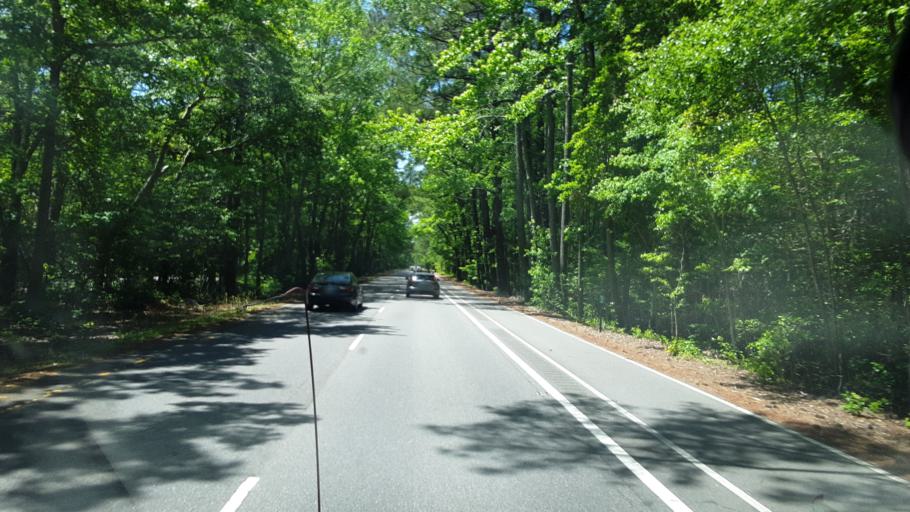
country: US
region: Virginia
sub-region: City of Virginia Beach
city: Virginia Beach
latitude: 36.9200
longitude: -76.0256
